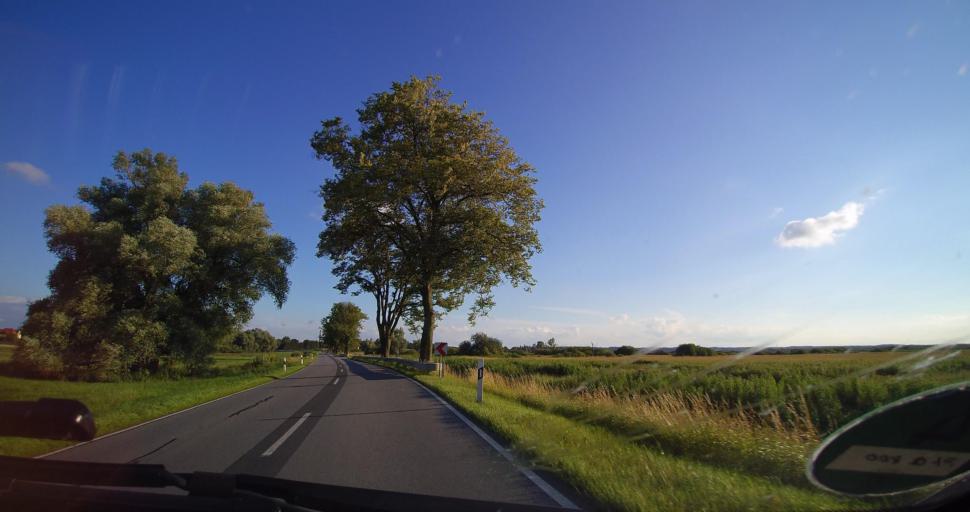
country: DE
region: Mecklenburg-Vorpommern
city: Tribsees
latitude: 54.1014
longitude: 12.7532
